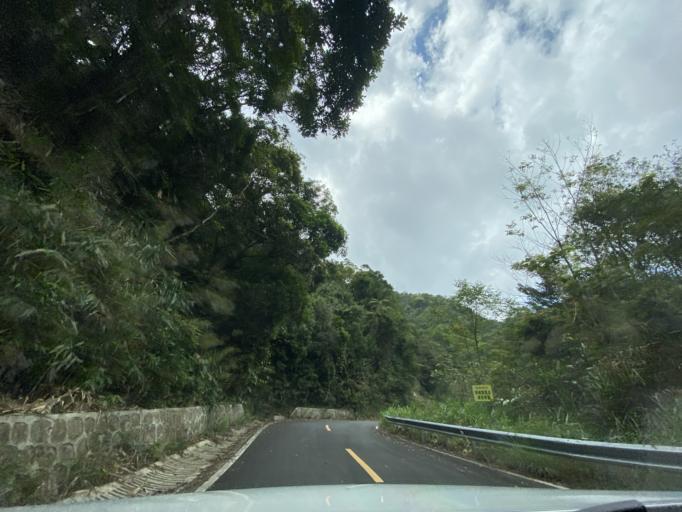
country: CN
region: Hainan
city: Benhao
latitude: 18.6867
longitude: 109.8791
